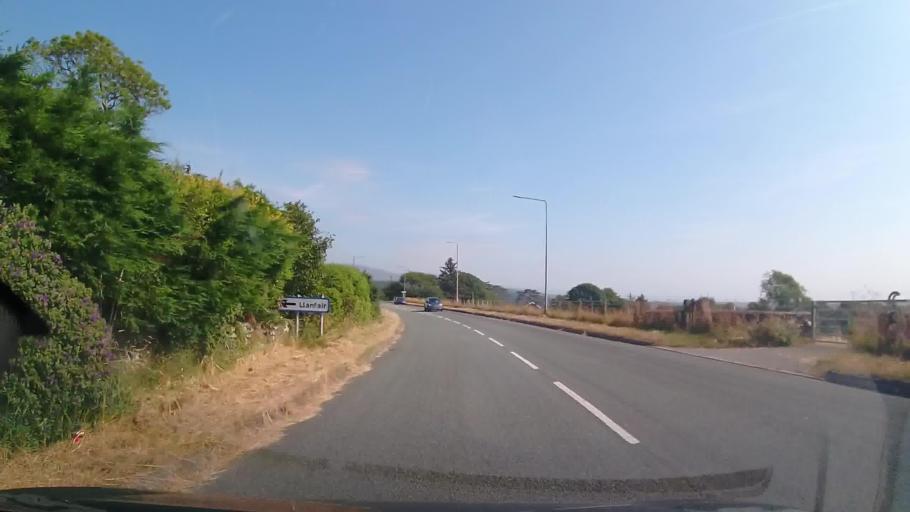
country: GB
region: Wales
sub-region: Gwynedd
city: Llanfair
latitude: 52.8401
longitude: -4.1146
